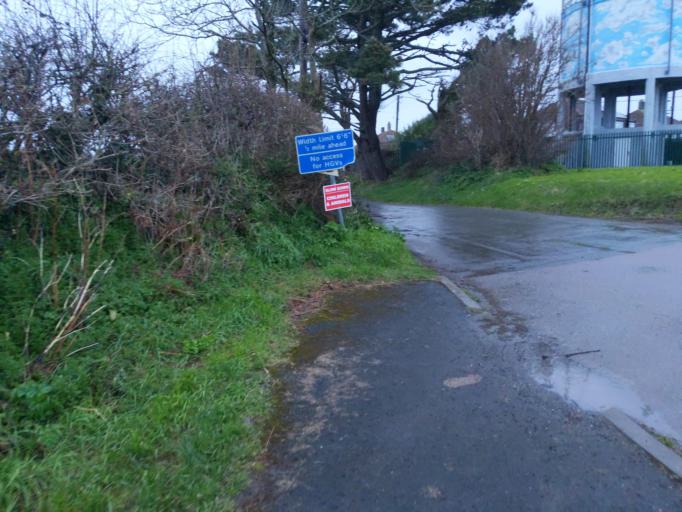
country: GB
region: England
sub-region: Devon
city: Wembury
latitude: 50.3218
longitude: -4.0324
